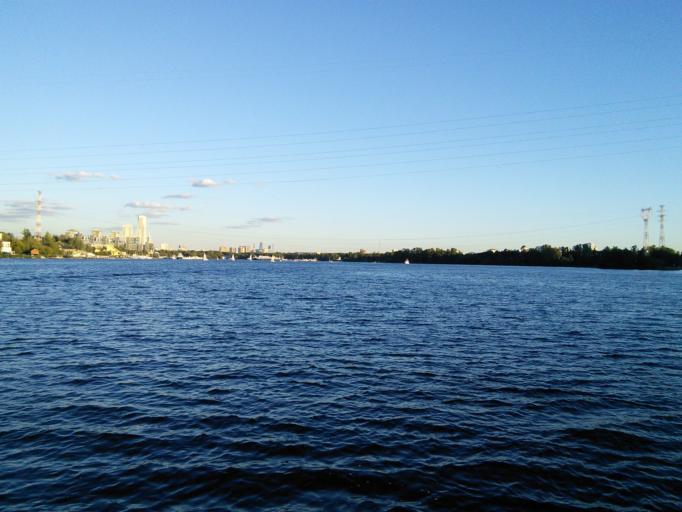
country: RU
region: Moskovskaya
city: Levoberezhnyy
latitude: 55.8431
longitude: 37.4692
